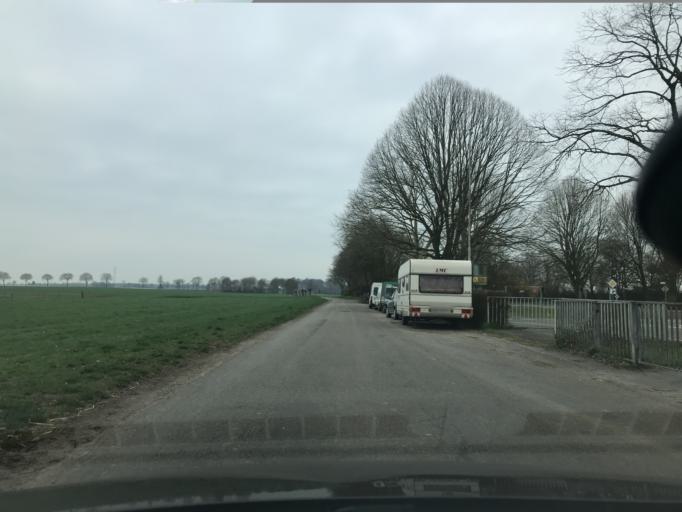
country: DE
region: North Rhine-Westphalia
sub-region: Regierungsbezirk Dusseldorf
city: Schwalmtal
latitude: 51.2502
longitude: 6.3068
